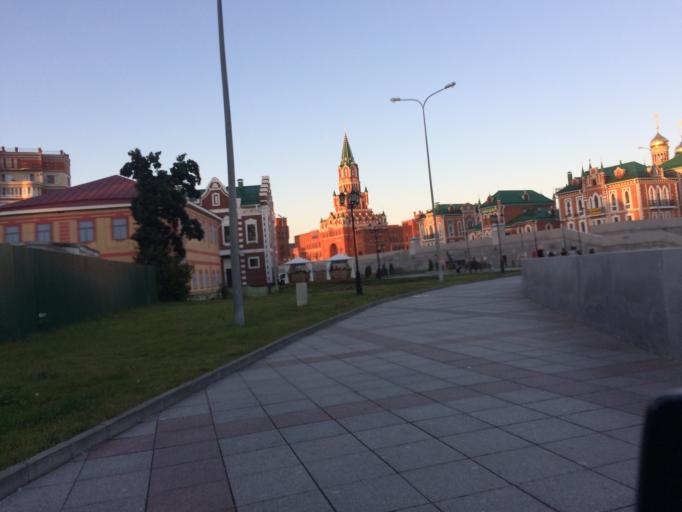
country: RU
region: Mariy-El
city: Yoshkar-Ola
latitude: 56.6326
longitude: 47.9002
